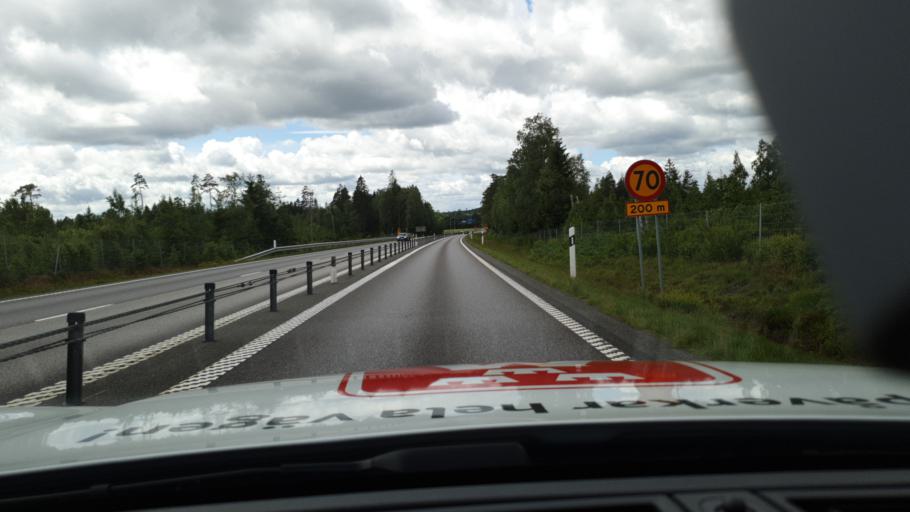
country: SE
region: Joenkoeping
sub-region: Varnamo Kommun
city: Rydaholm
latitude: 56.8761
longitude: 14.1814
